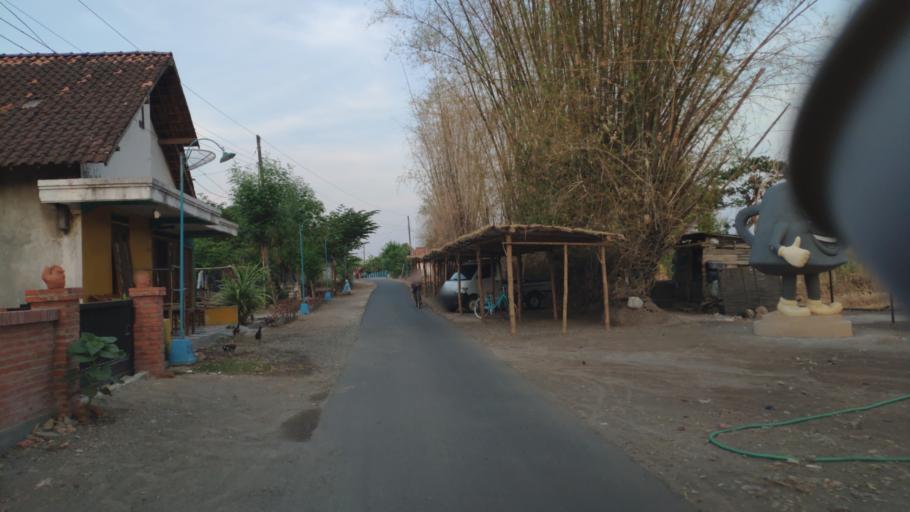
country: ID
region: Central Java
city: Nglaroh
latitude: -6.9627
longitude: 111.4508
